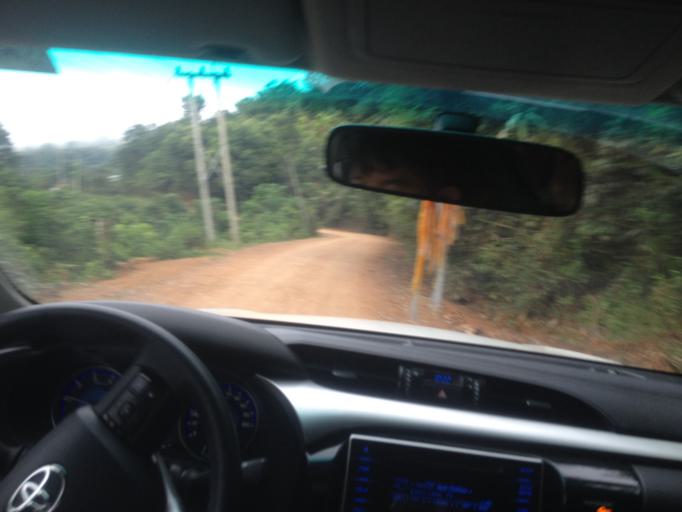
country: TH
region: Nan
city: Chaloem Phra Kiat
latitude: 19.9788
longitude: 101.1423
